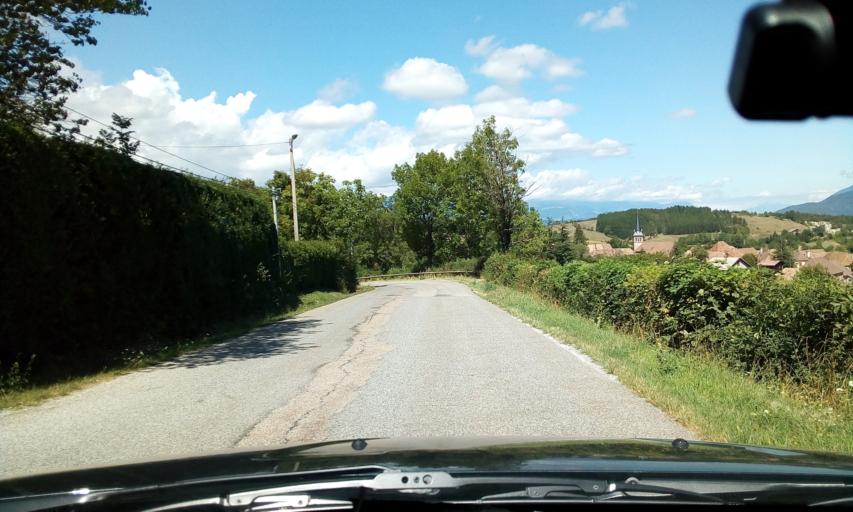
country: FR
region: Rhone-Alpes
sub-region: Departement de l'Isere
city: Mens
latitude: 44.7538
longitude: 5.6760
